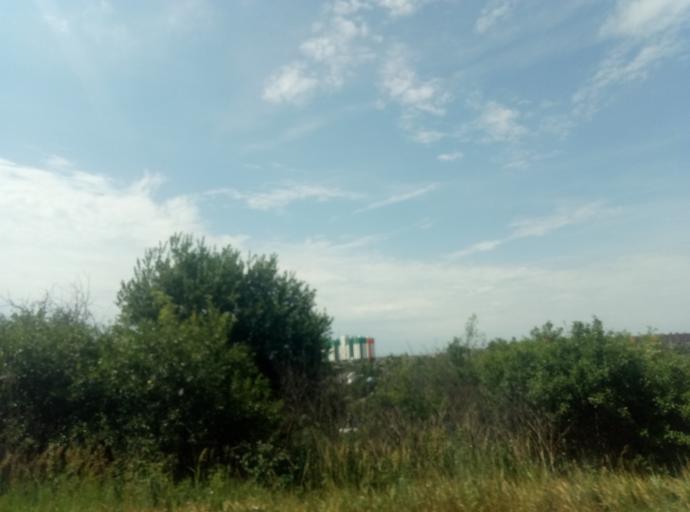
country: RU
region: Tula
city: Kireyevsk
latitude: 53.9216
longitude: 37.9515
